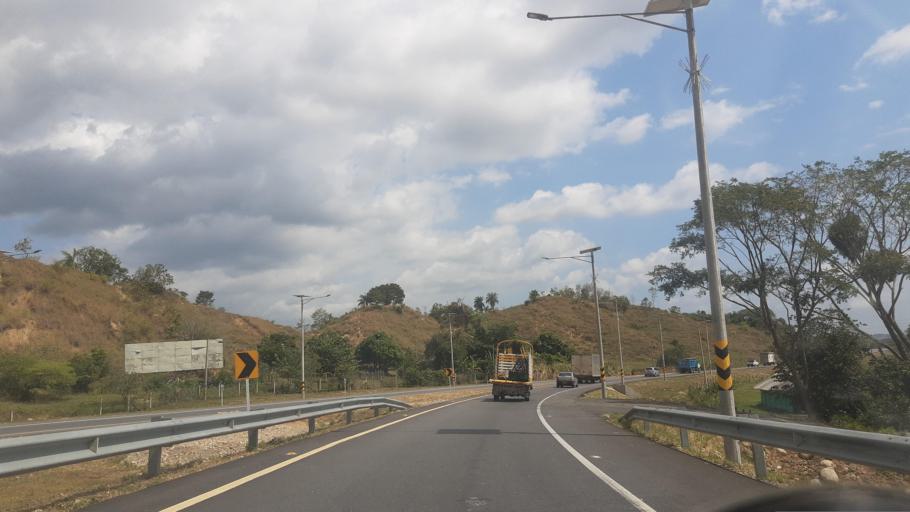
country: CO
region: Casanare
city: Tauramena
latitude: 5.0178
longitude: -72.6714
